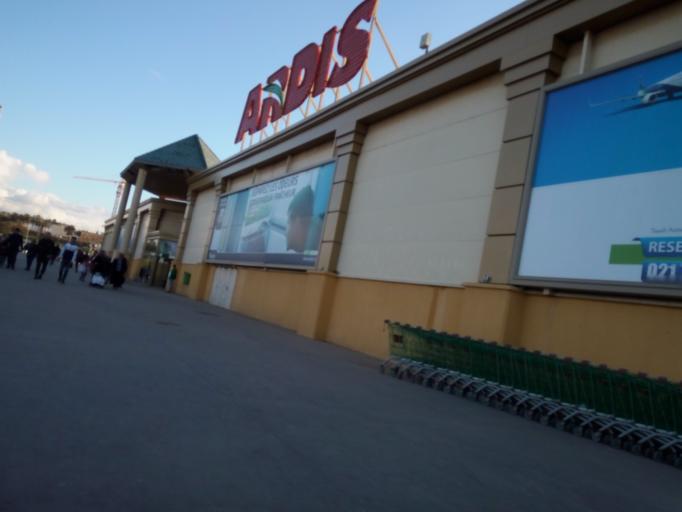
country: DZ
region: Alger
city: Bab Ezzouar
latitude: 36.7388
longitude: 3.1435
